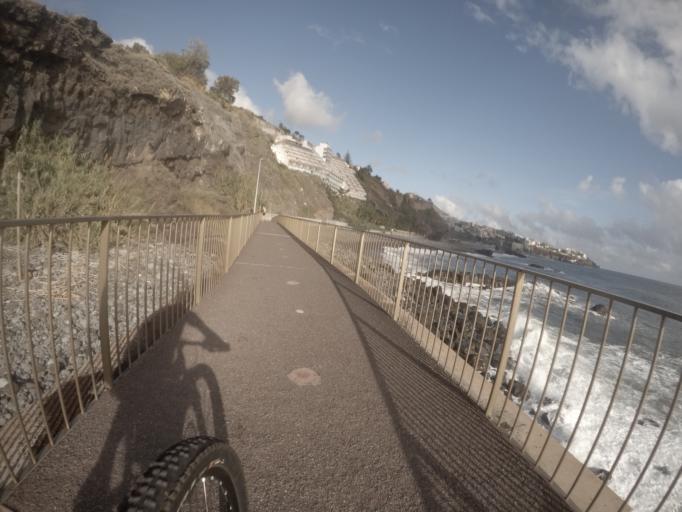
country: PT
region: Madeira
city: Camara de Lobos
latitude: 32.6430
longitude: -16.9619
